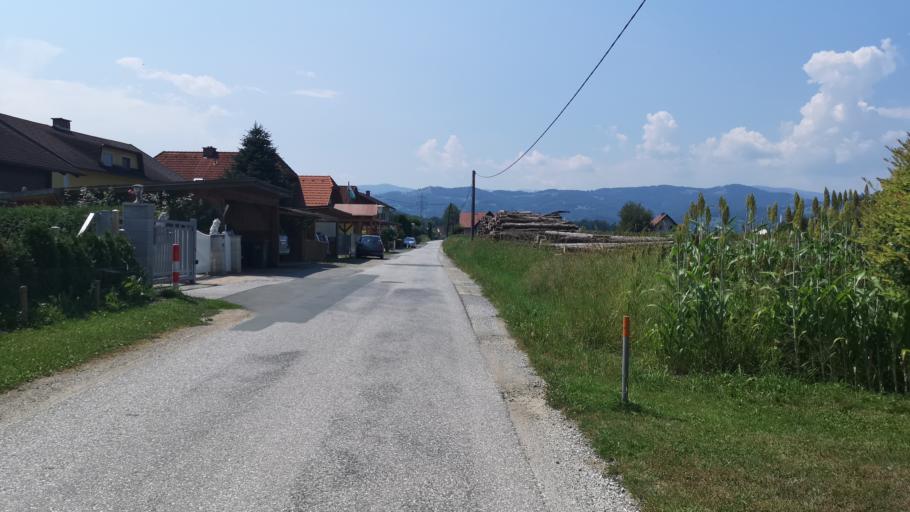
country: AT
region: Styria
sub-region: Politischer Bezirk Deutschlandsberg
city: Deutschlandsberg
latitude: 46.8189
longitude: 15.2638
